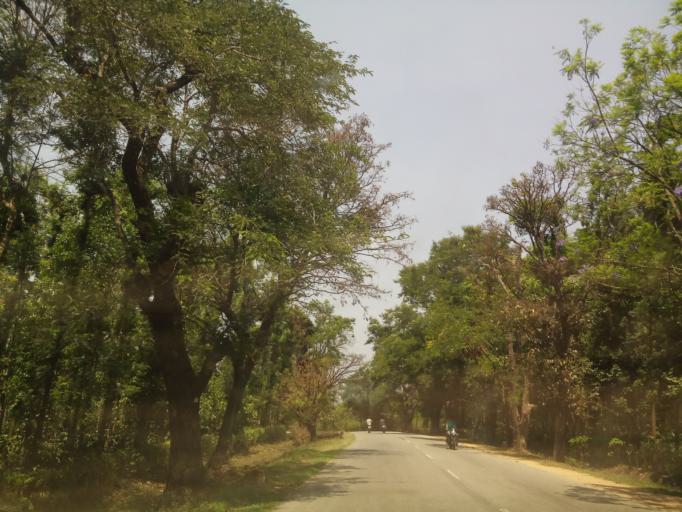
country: IN
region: Karnataka
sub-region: Hassan
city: Sakleshpur
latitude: 12.9524
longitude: 75.8668
